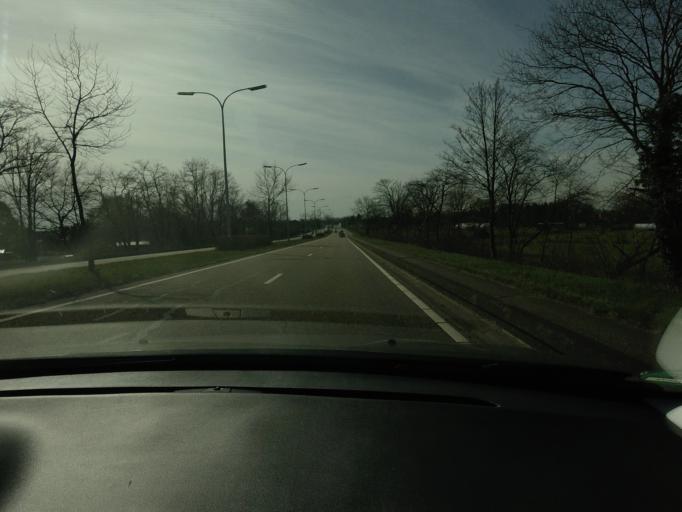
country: BE
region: Flanders
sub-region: Provincie Limburg
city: Zonhoven
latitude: 51.0003
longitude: 5.3649
